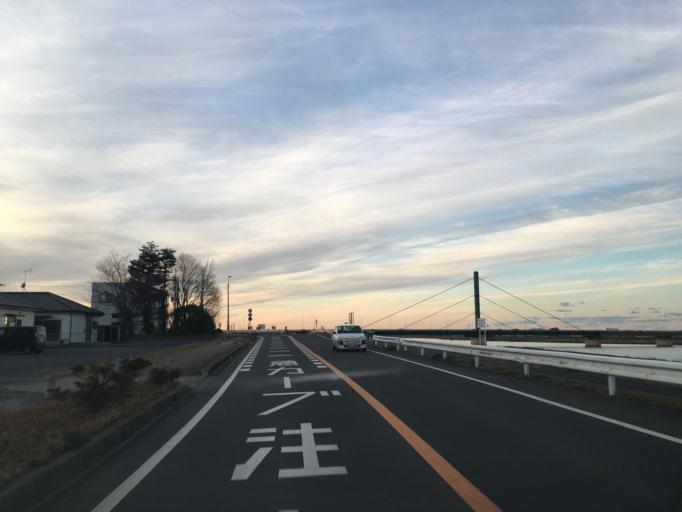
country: JP
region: Chiba
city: Katori-shi
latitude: 35.9052
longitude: 140.4948
